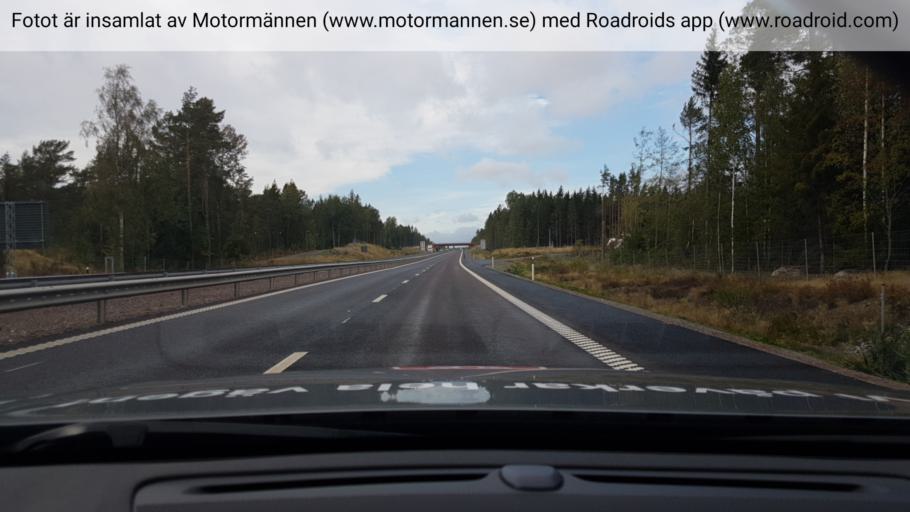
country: SE
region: Vaermland
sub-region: Hammaro Kommun
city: Skoghall
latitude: 59.3812
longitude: 13.3844
